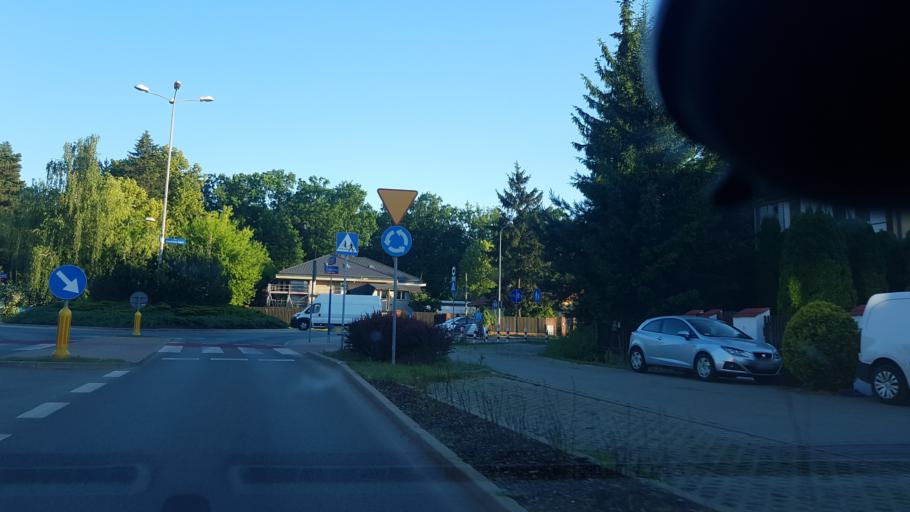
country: PL
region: Masovian Voivodeship
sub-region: Warszawa
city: Wesola
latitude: 52.2182
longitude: 21.2226
